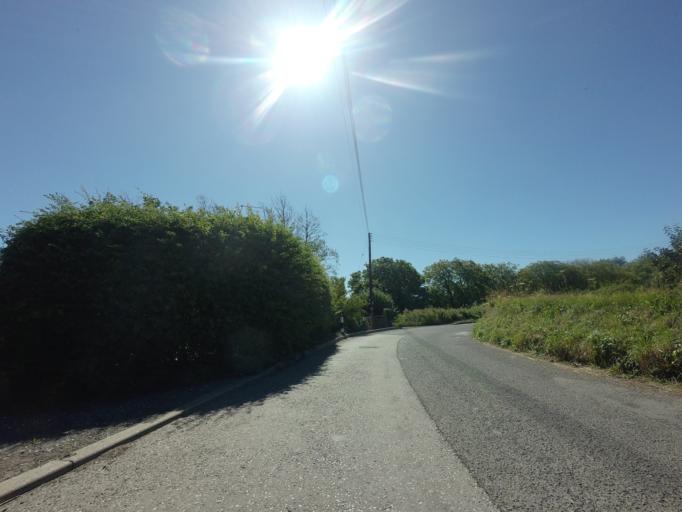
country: GB
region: England
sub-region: Kent
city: Ash
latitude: 51.3011
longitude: 1.2393
